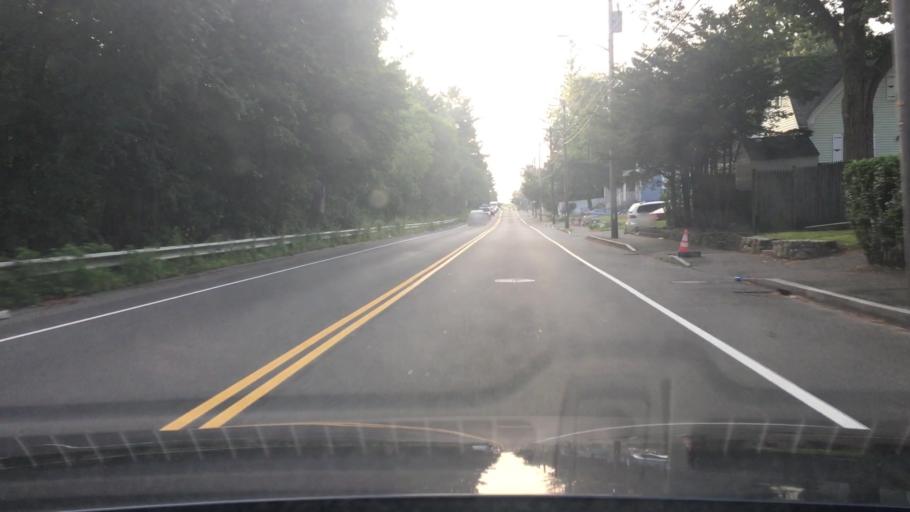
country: US
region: Massachusetts
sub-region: Essex County
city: Saugus
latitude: 42.4761
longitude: -70.9993
